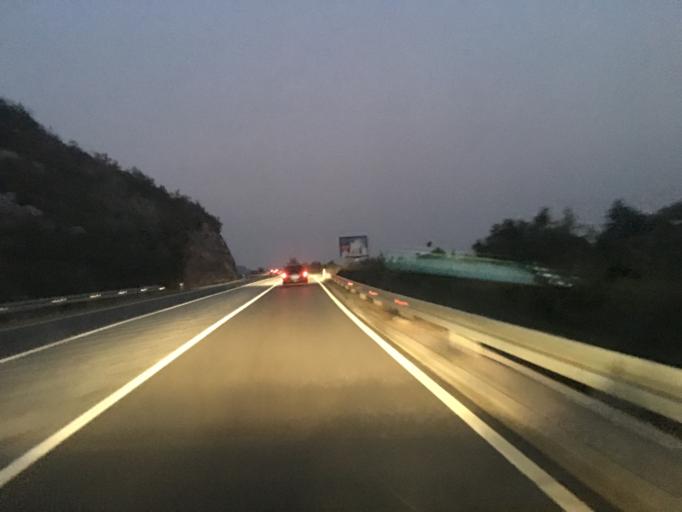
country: ME
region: Cetinje
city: Cetinje
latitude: 42.3808
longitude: 19.0189
